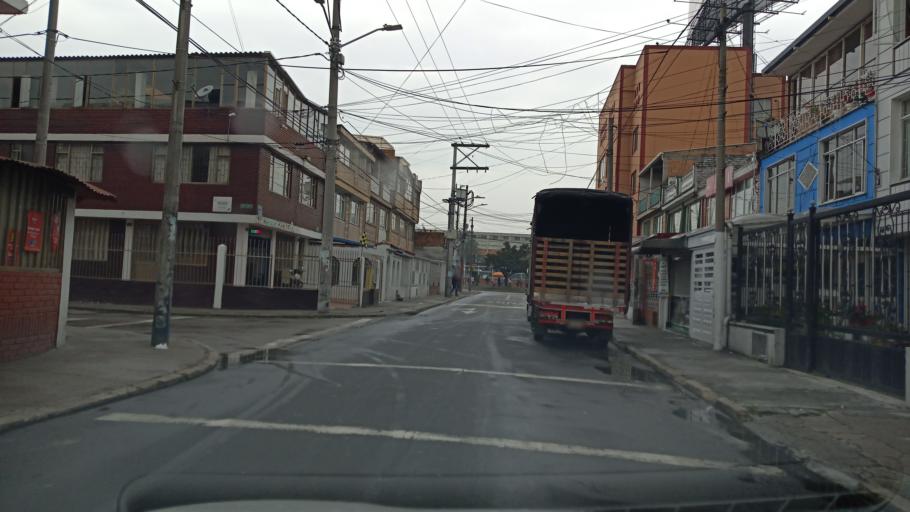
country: CO
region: Bogota D.C.
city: Bogota
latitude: 4.5945
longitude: -74.1135
